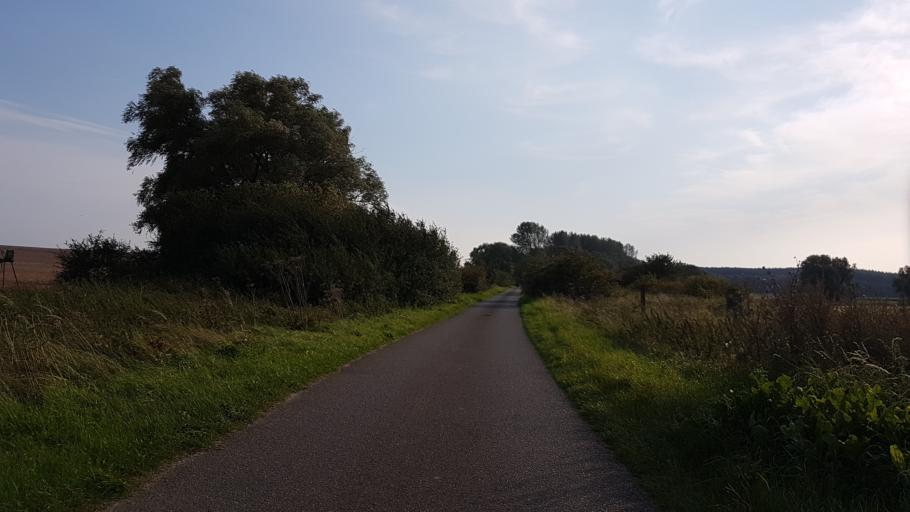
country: DE
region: Mecklenburg-Vorpommern
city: Sagard
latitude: 54.5138
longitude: 13.5298
